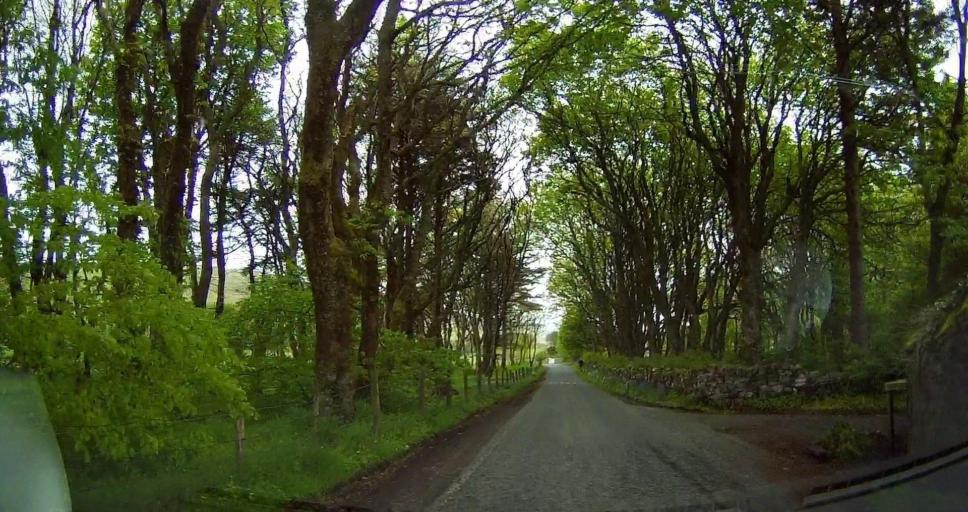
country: GB
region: Scotland
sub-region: Shetland Islands
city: Lerwick
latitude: 60.2710
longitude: -1.2869
